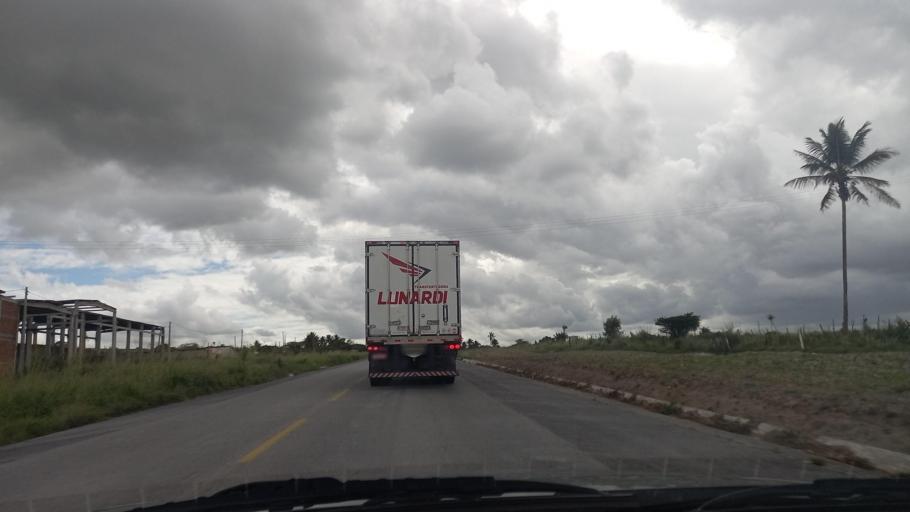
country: BR
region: Pernambuco
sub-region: Lajedo
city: Lajedo
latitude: -8.6653
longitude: -36.3612
